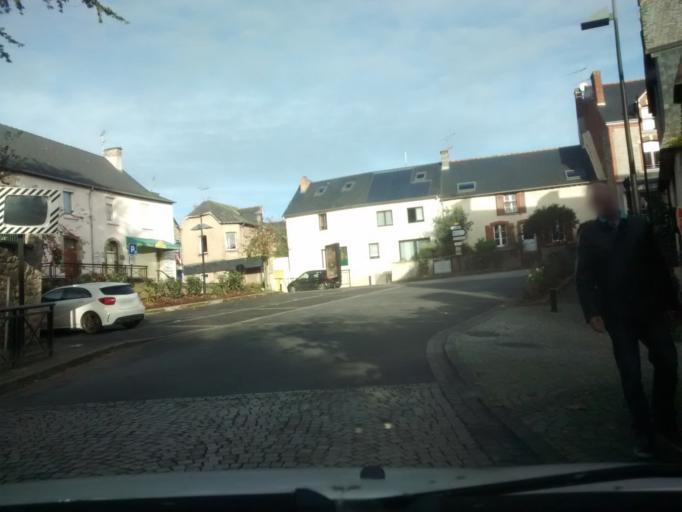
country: FR
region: Brittany
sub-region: Departement d'Ille-et-Vilaine
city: Acigne
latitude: 48.1315
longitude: -1.5356
